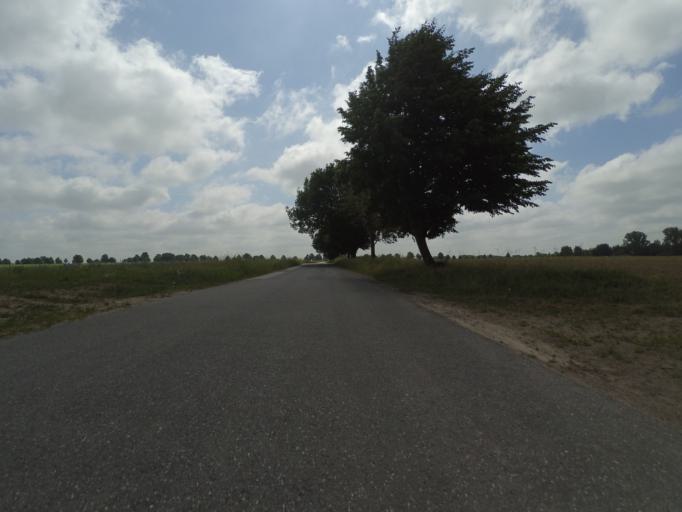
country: DE
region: Mecklenburg-Vorpommern
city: Demen
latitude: 53.5682
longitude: 11.8356
